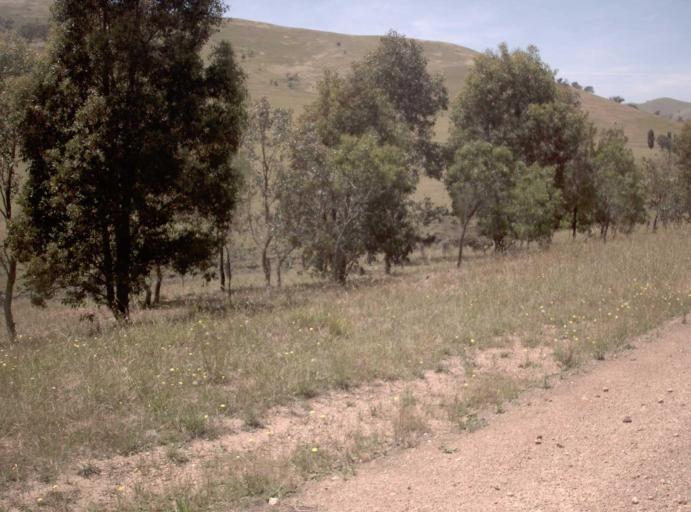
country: AU
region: Victoria
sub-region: East Gippsland
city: Bairnsdale
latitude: -37.3503
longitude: 147.8026
